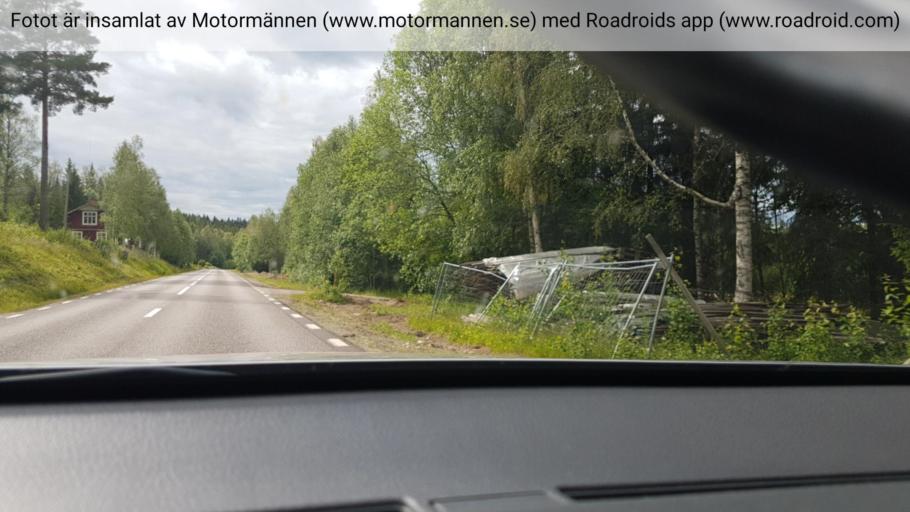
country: NO
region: Hedmark
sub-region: Trysil
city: Innbygda
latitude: 60.8997
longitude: 12.5828
